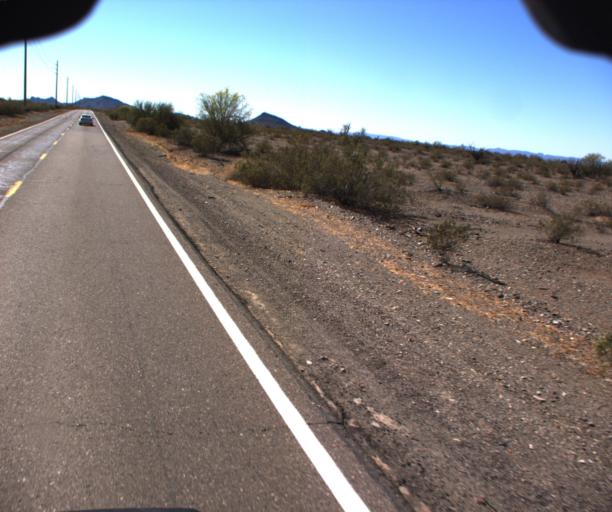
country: US
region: Arizona
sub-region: La Paz County
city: Salome
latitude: 33.7597
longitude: -113.7807
